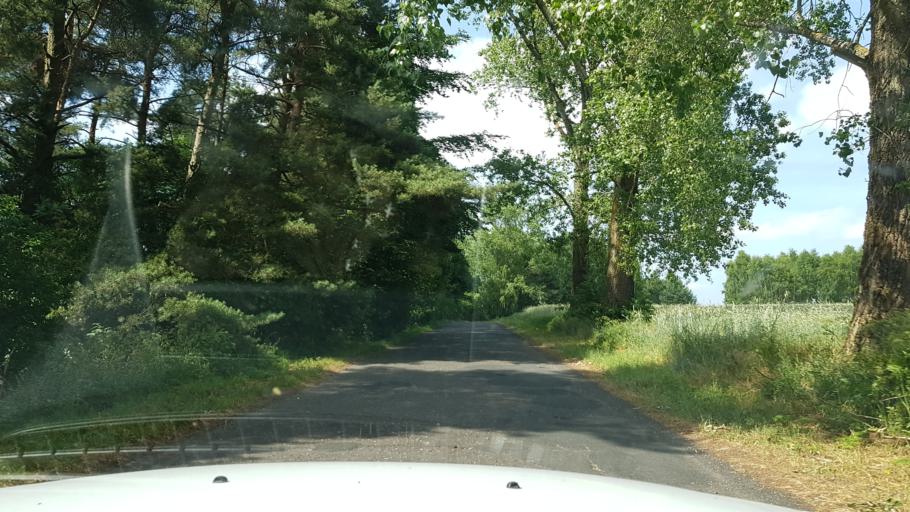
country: PL
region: West Pomeranian Voivodeship
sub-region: Powiat goleniowski
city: Mosty
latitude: 53.5669
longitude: 14.9744
